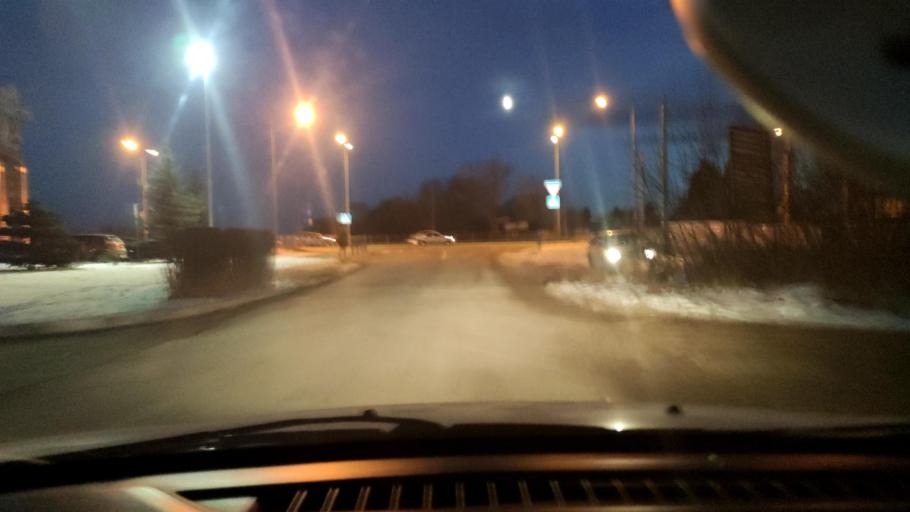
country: RU
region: Perm
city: Kondratovo
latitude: 57.9464
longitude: 56.0782
